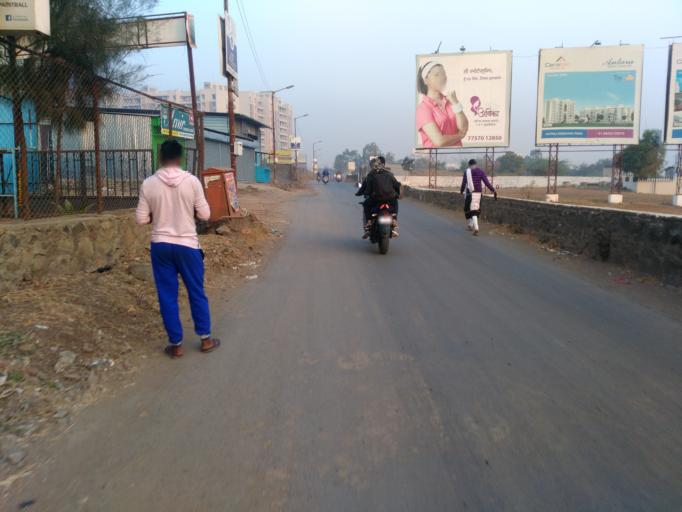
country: IN
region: Maharashtra
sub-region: Pune Division
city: Pune
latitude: 18.4478
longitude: 73.8855
